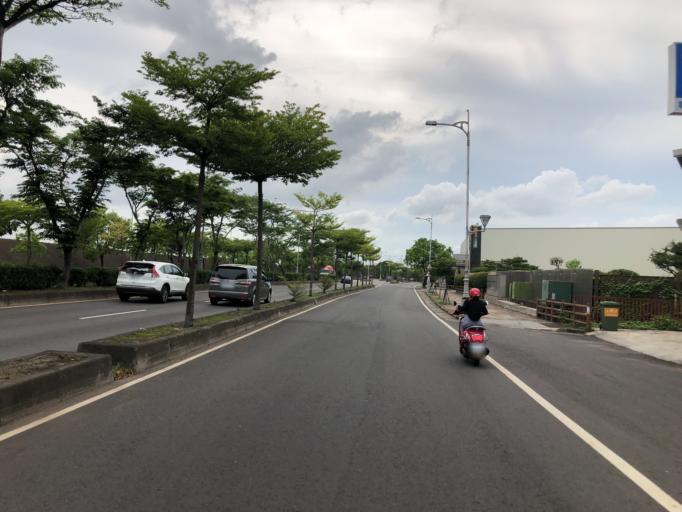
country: TW
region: Taiwan
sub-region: Taichung City
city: Taichung
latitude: 24.0942
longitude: 120.6378
